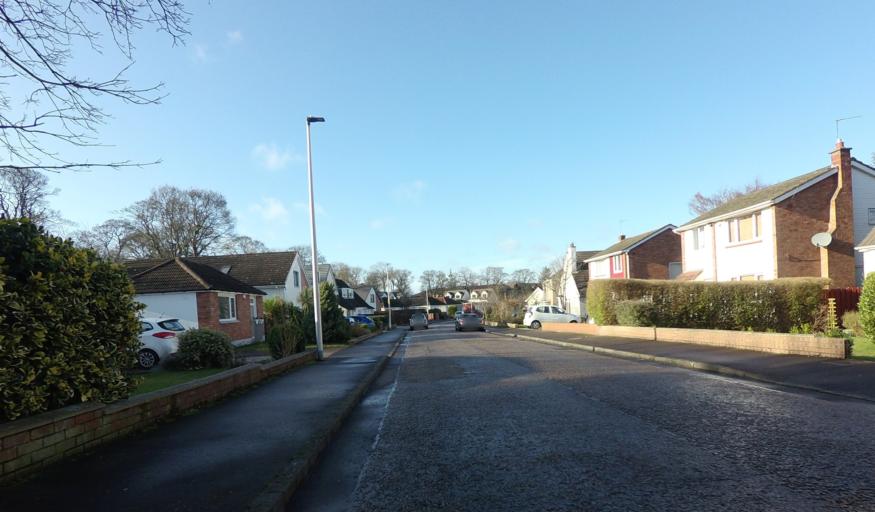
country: GB
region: Scotland
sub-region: Edinburgh
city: Currie
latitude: 55.9613
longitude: -3.2963
